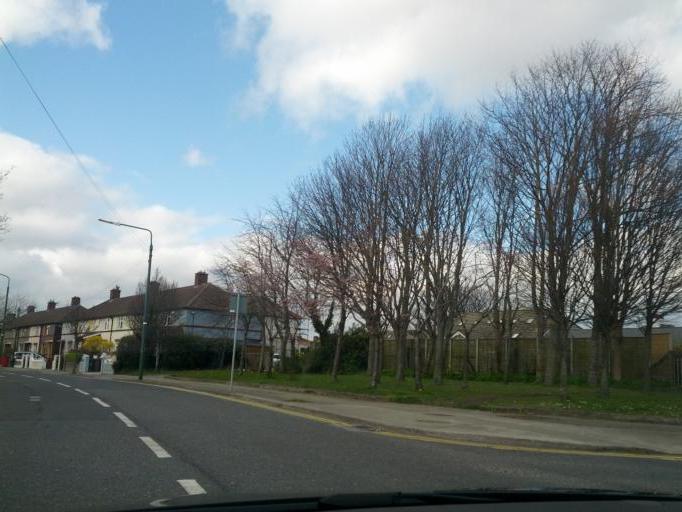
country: IE
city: Donnycarney
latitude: 53.3720
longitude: -6.2078
